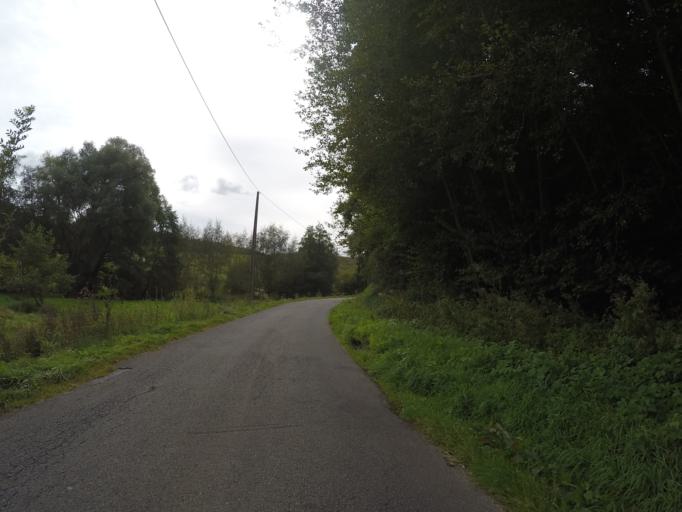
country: BE
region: Wallonia
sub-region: Province de Namur
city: Dinant
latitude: 50.2728
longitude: 4.9860
